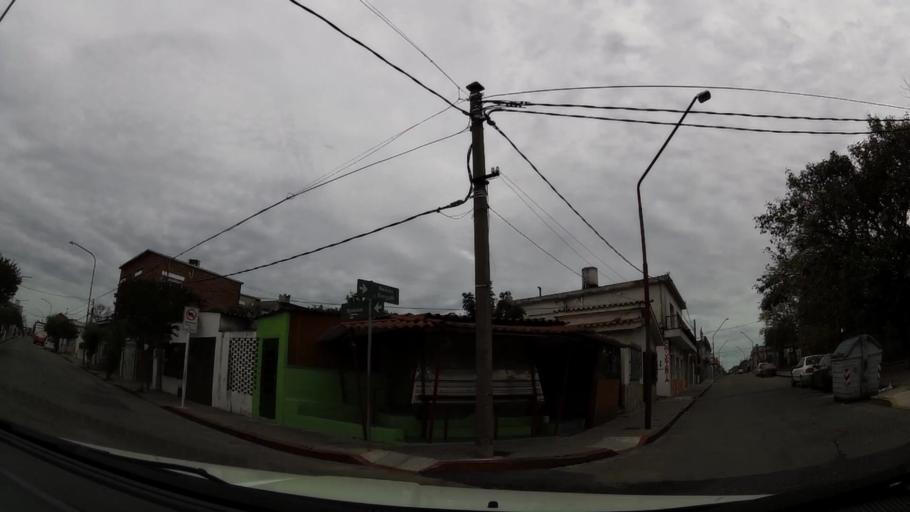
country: UY
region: Maldonado
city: Maldonado
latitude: -34.9047
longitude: -54.9556
